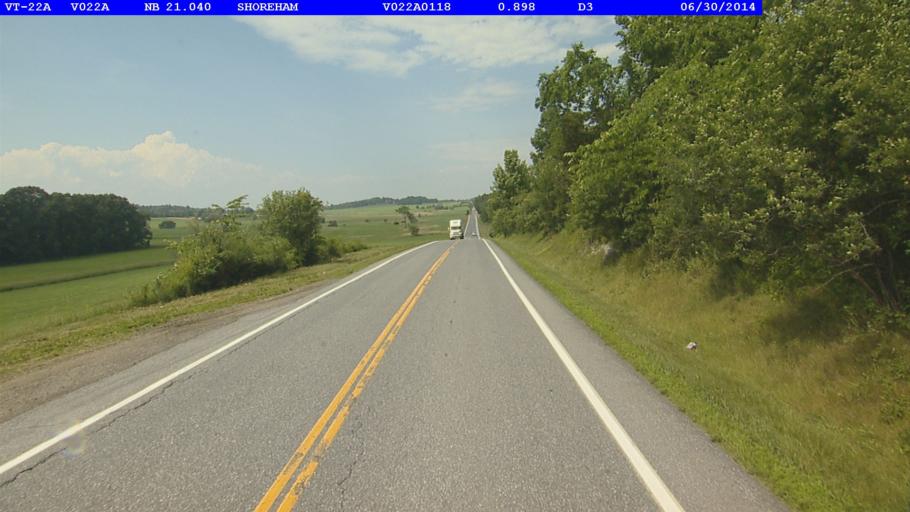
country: US
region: New York
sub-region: Essex County
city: Ticonderoga
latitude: 43.8624
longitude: -73.3096
